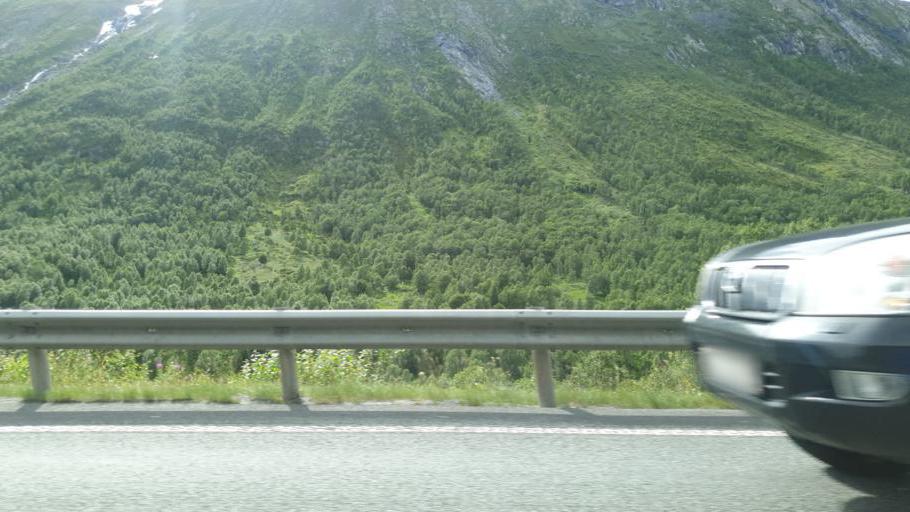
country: NO
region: Sor-Trondelag
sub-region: Oppdal
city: Oppdal
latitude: 62.4160
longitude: 9.6360
